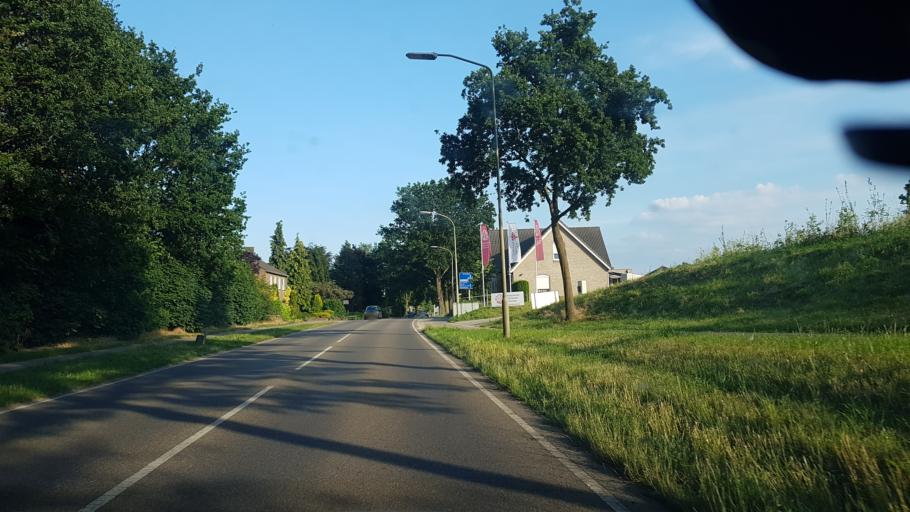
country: NL
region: Gelderland
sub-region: Gemeente Groesbeek
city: Groesbeek
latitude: 51.7689
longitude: 5.9350
